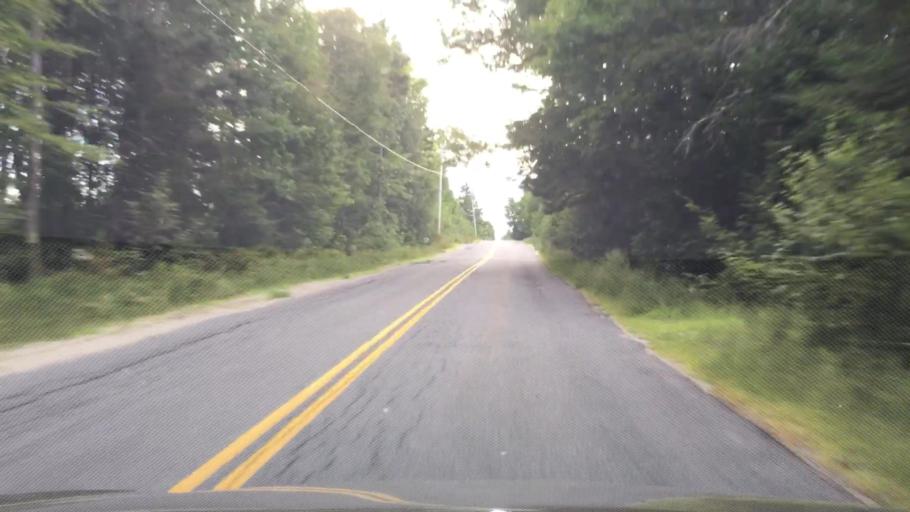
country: US
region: Maine
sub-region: Hancock County
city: Penobscot
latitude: 44.4443
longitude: -68.6310
